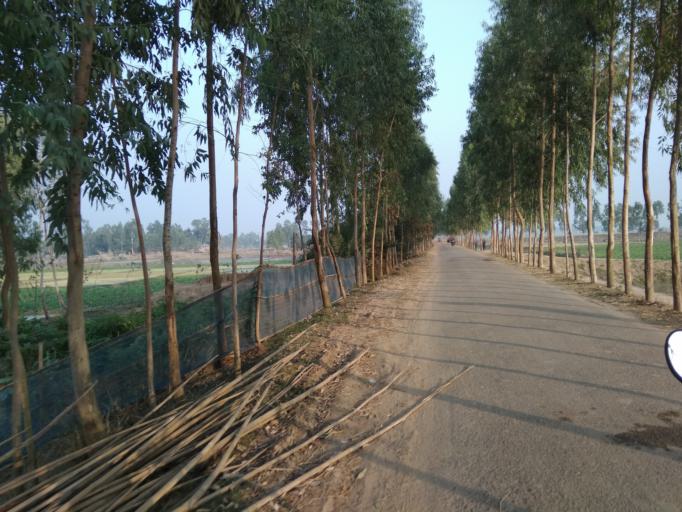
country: BD
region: Rajshahi
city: Bogra
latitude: 24.4766
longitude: 89.2673
